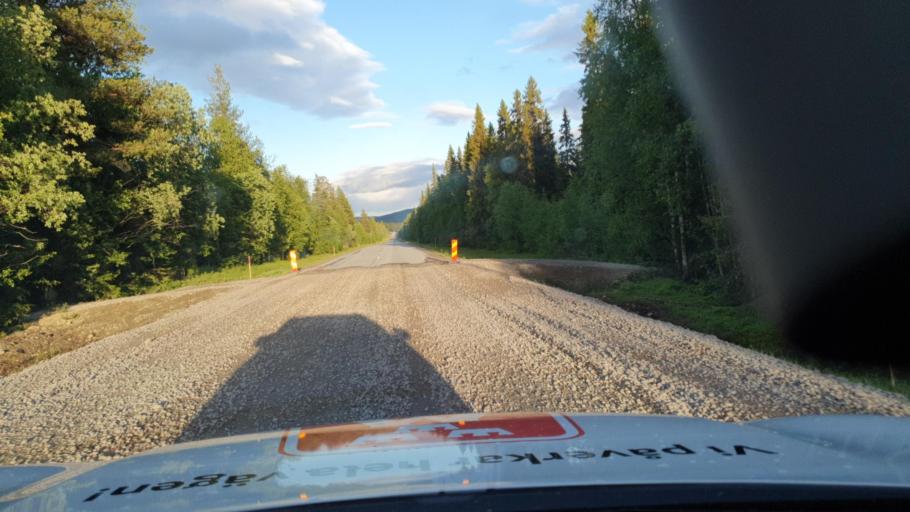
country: SE
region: Vaesterbotten
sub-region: Lycksele Kommun
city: Soderfors
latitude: 64.7064
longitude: 17.7190
